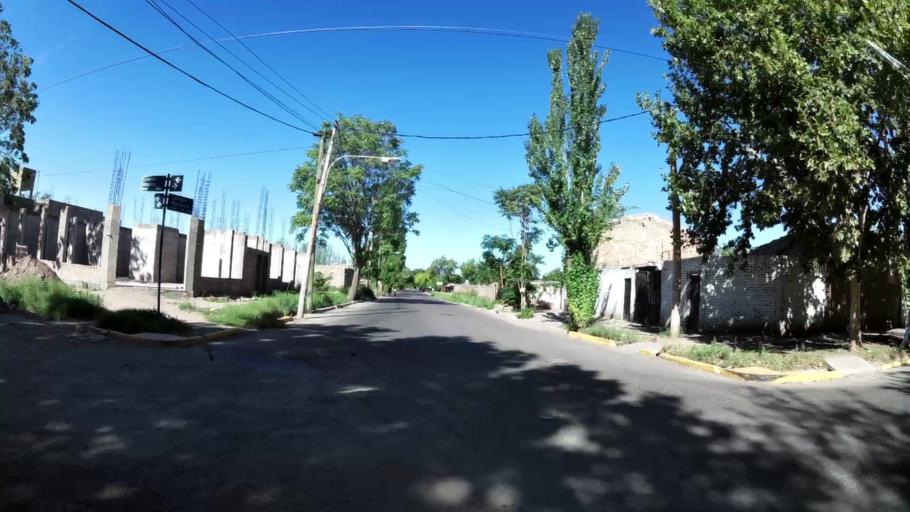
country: AR
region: Mendoza
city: Las Heras
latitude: -32.8466
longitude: -68.8203
